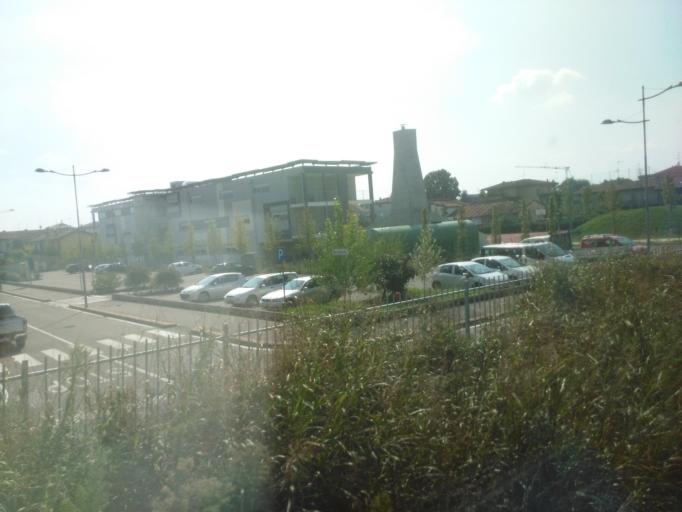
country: IT
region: Lombardy
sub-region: Provincia di Bergamo
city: Romano di Lombardia
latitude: 45.5239
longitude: 9.7601
